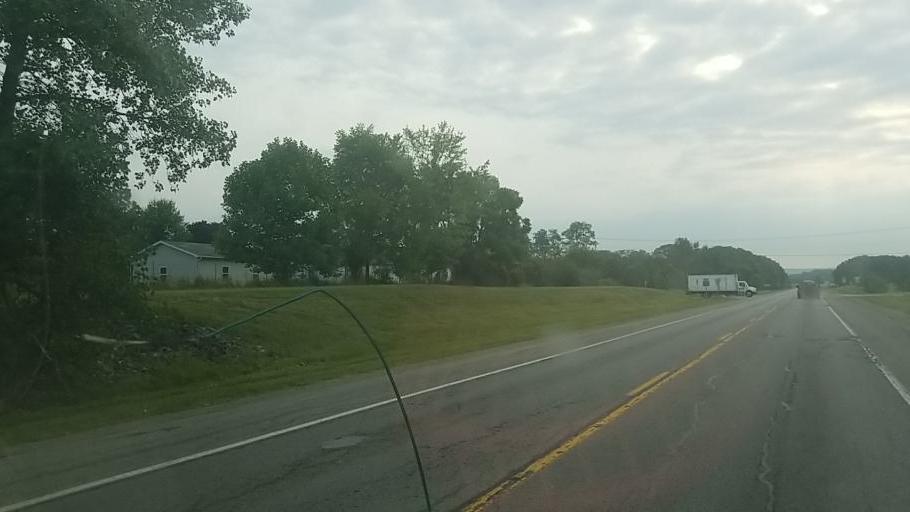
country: US
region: Ohio
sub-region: Ashland County
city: Ashland
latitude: 40.8870
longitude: -82.3186
